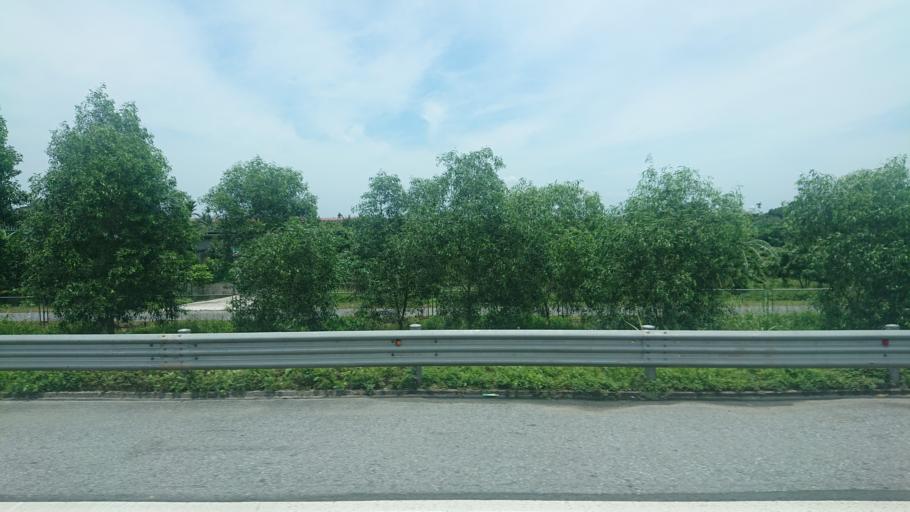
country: VN
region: Hai Duong
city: Tu Ky
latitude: 20.8270
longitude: 106.4594
